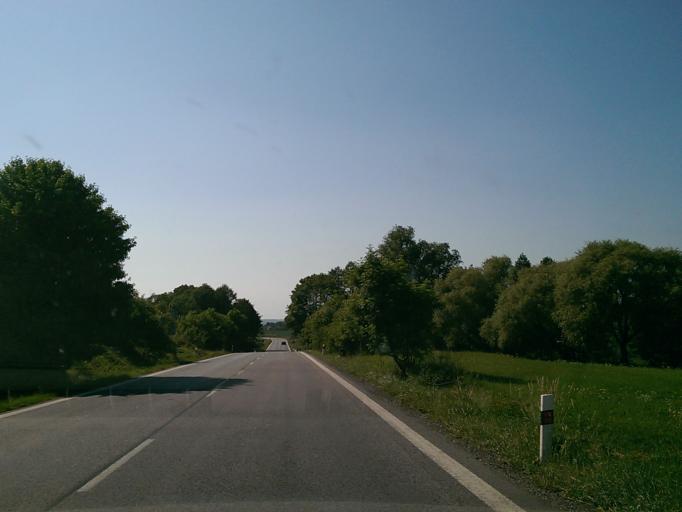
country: CZ
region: Kralovehradecky
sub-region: Okres Jicin
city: Jicin
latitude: 50.4934
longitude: 15.3150
